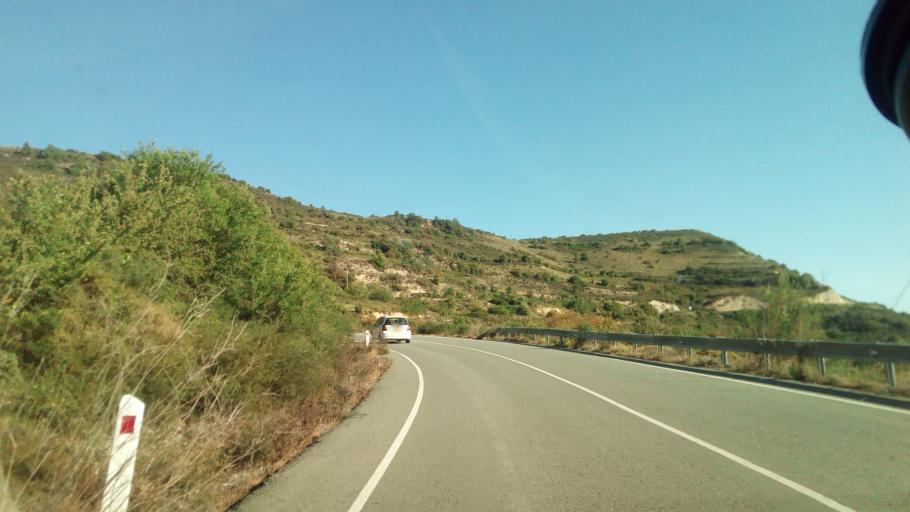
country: CY
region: Limassol
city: Pachna
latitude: 34.8617
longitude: 32.7601
